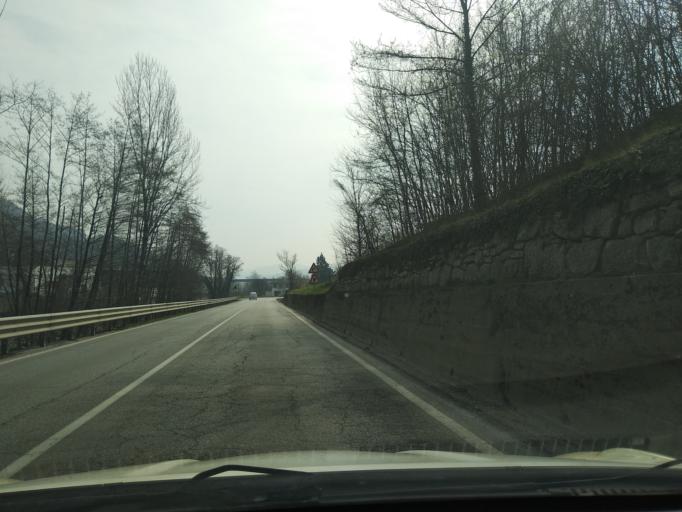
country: IT
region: Veneto
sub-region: Provincia di Vicenza
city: Chiampo
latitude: 45.5593
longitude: 11.2699
